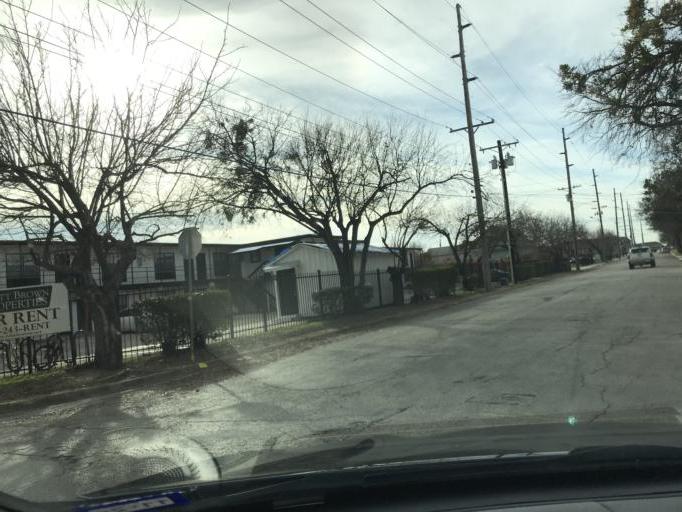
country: US
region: Texas
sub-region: Denton County
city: Denton
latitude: 33.2137
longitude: -97.1580
